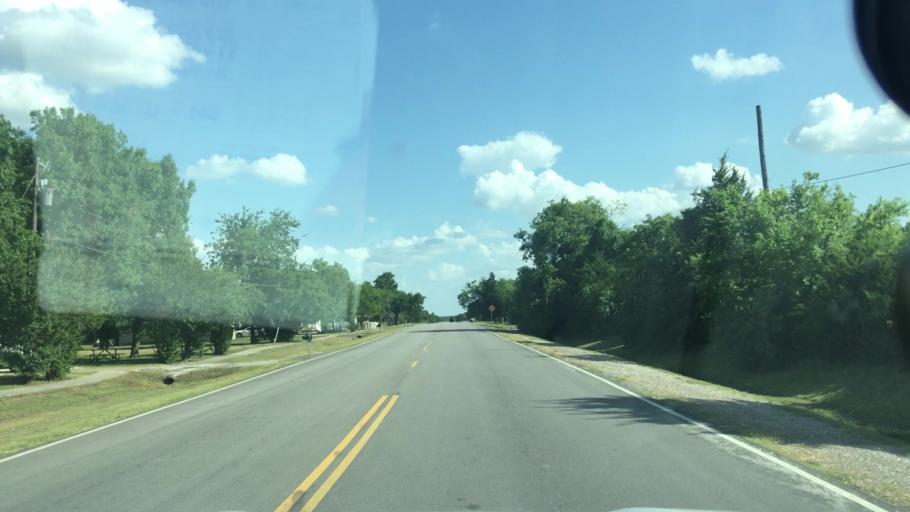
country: US
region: Texas
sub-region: Dallas County
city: Lancaster
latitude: 32.6035
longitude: -96.7478
